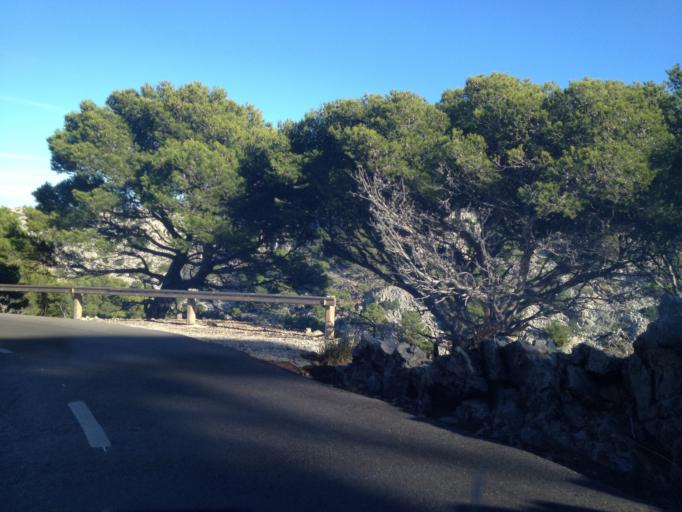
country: ES
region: Balearic Islands
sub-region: Illes Balears
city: Alcudia
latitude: 39.9535
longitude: 3.2028
